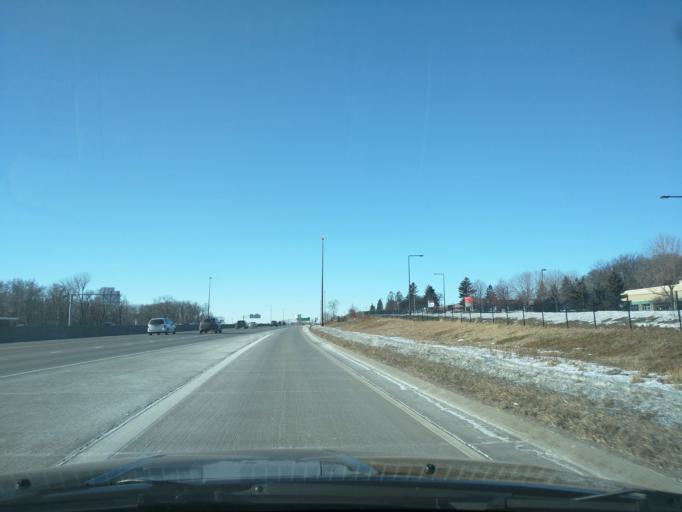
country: US
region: Minnesota
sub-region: Hennepin County
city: Edina
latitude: 44.8596
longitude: -93.4021
